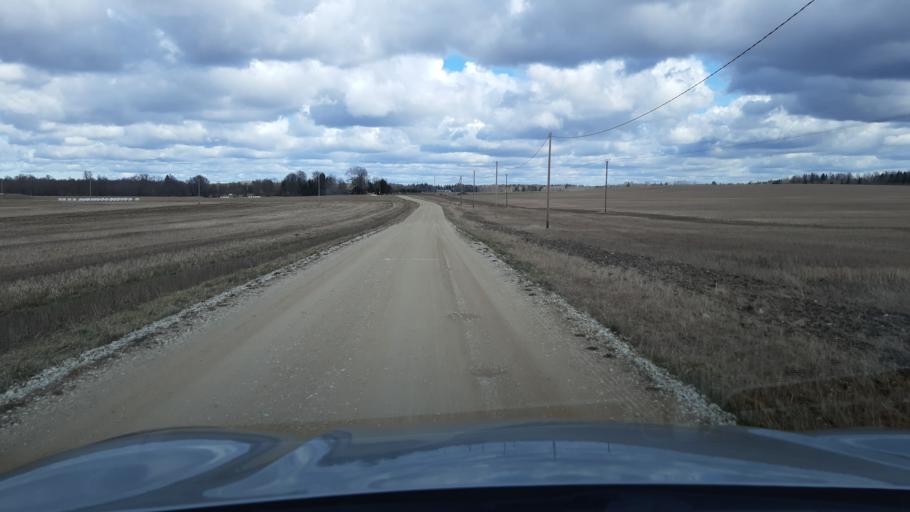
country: EE
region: Harju
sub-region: Rae vald
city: Vaida
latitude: 59.0816
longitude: 25.1269
